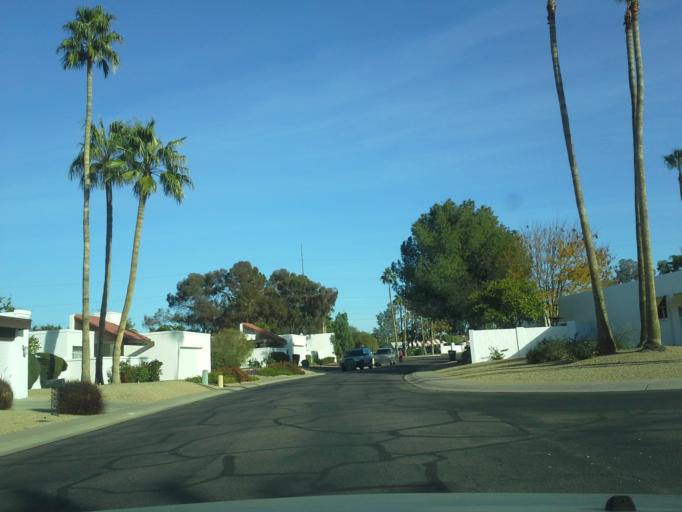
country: US
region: Arizona
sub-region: Maricopa County
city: Glendale
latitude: 33.6145
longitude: -112.0674
